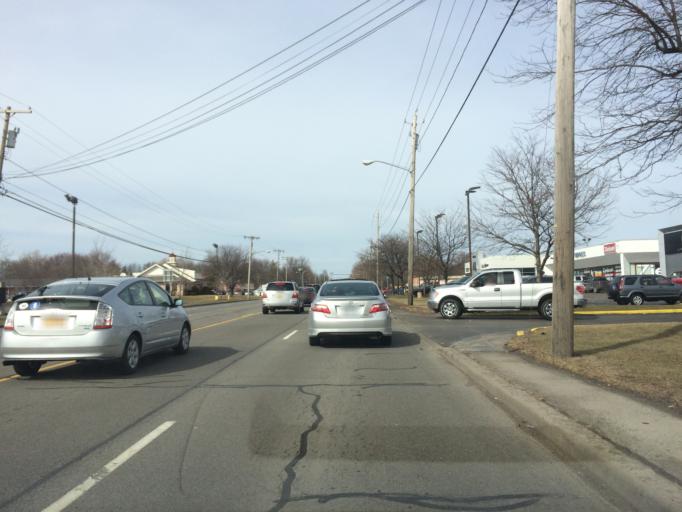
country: US
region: New York
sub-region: Monroe County
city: Rochester
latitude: 43.1020
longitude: -77.6288
